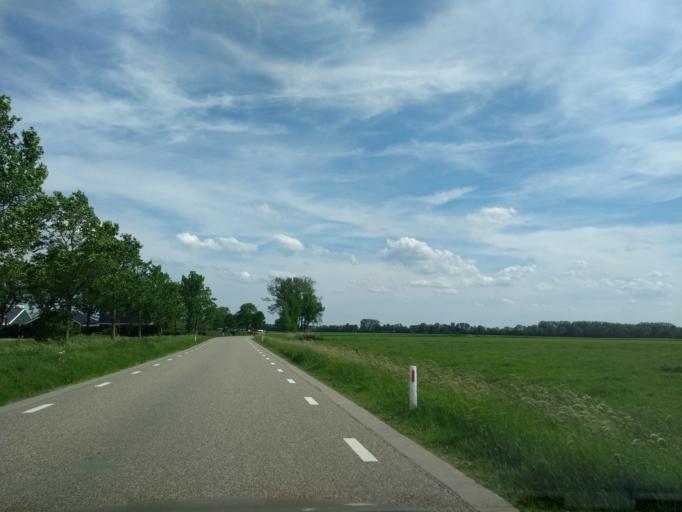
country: NL
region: Groningen
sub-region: Gemeente Zuidhorn
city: Aduard
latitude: 53.2696
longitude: 6.4342
